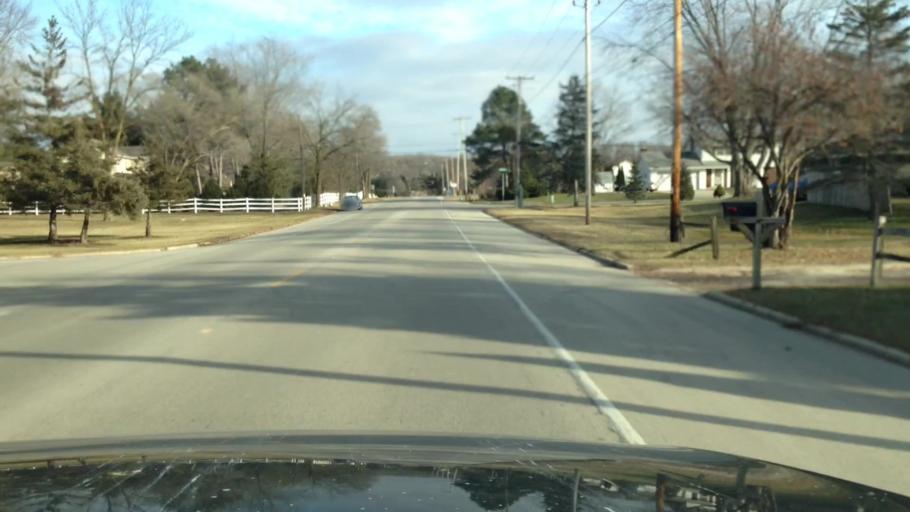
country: US
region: Wisconsin
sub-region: Waukesha County
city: Muskego
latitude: 42.9300
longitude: -88.1414
